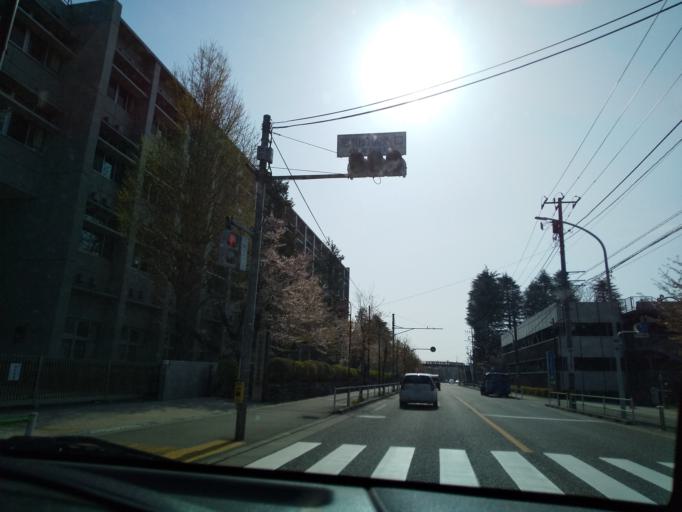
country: JP
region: Tokyo
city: Hino
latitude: 35.7037
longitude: 139.3869
